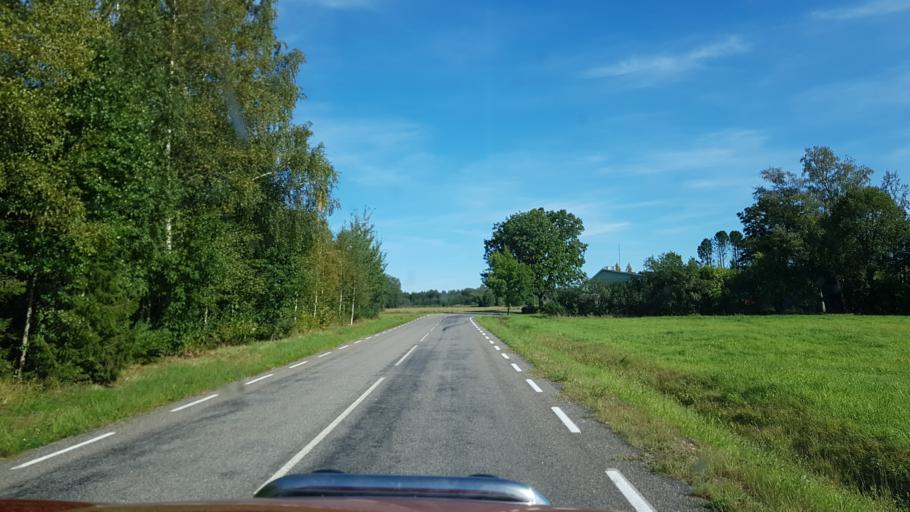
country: EE
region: Paernumaa
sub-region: Saarde vald
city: Kilingi-Nomme
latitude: 58.1412
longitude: 24.9878
